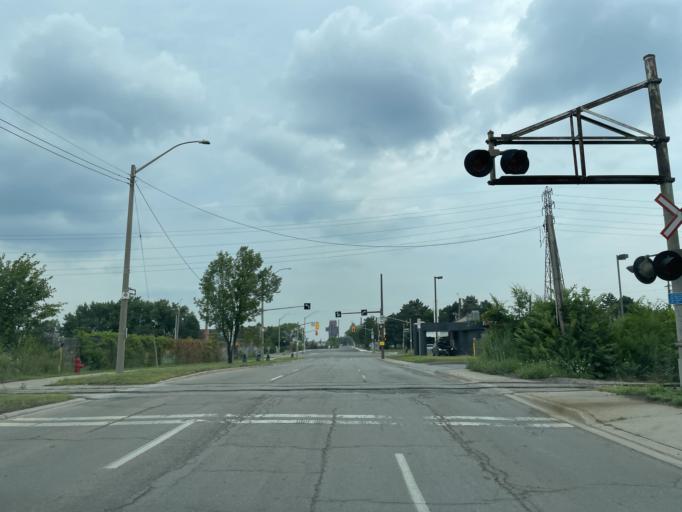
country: CA
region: Ontario
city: Hamilton
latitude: 43.2645
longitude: -79.8328
